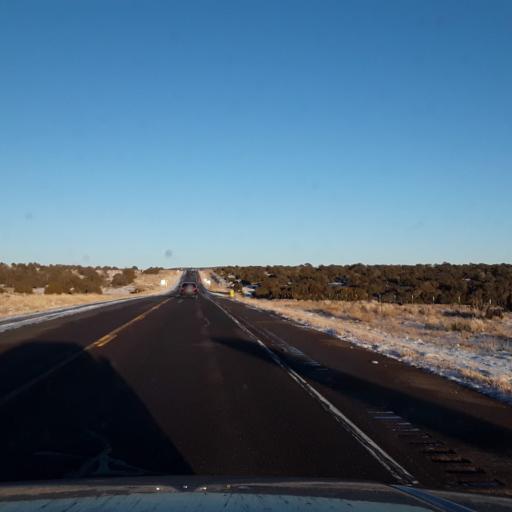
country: US
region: New Mexico
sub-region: Lincoln County
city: Carrizozo
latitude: 34.2325
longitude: -105.6235
